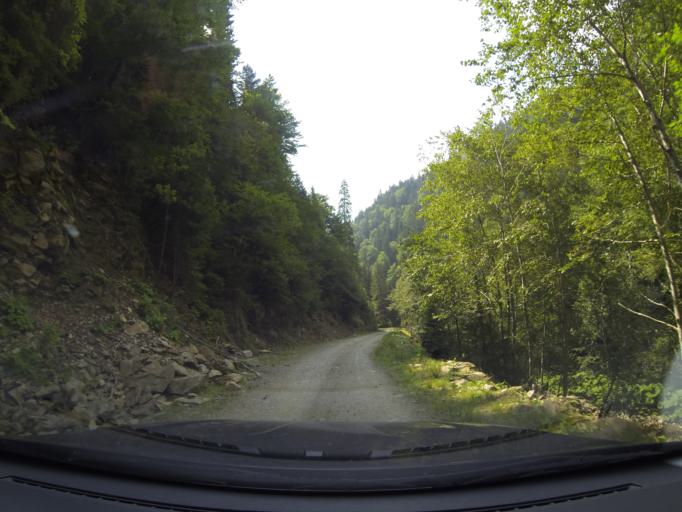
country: RO
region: Arges
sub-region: Comuna Arefu
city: Arefu
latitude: 45.5146
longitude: 24.6703
